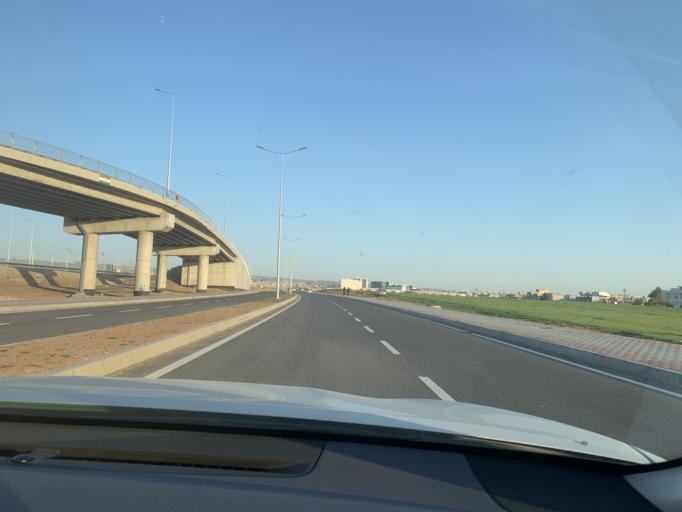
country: IQ
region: Arbil
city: Erbil
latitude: 36.2802
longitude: 44.0646
